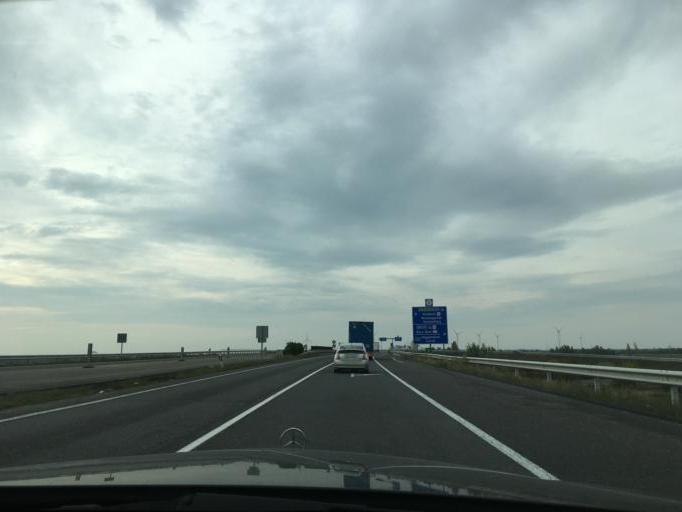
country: HU
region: Gyor-Moson-Sopron
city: Rajka
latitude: 47.9069
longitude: 17.1829
